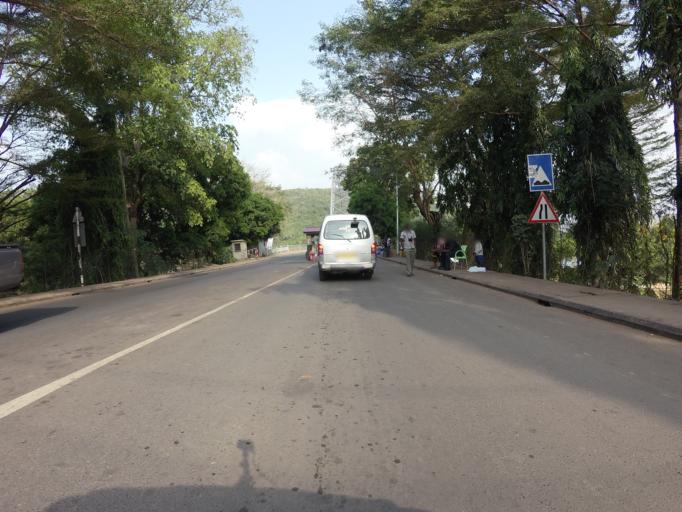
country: GH
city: Akropong
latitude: 6.2394
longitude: 0.0932
